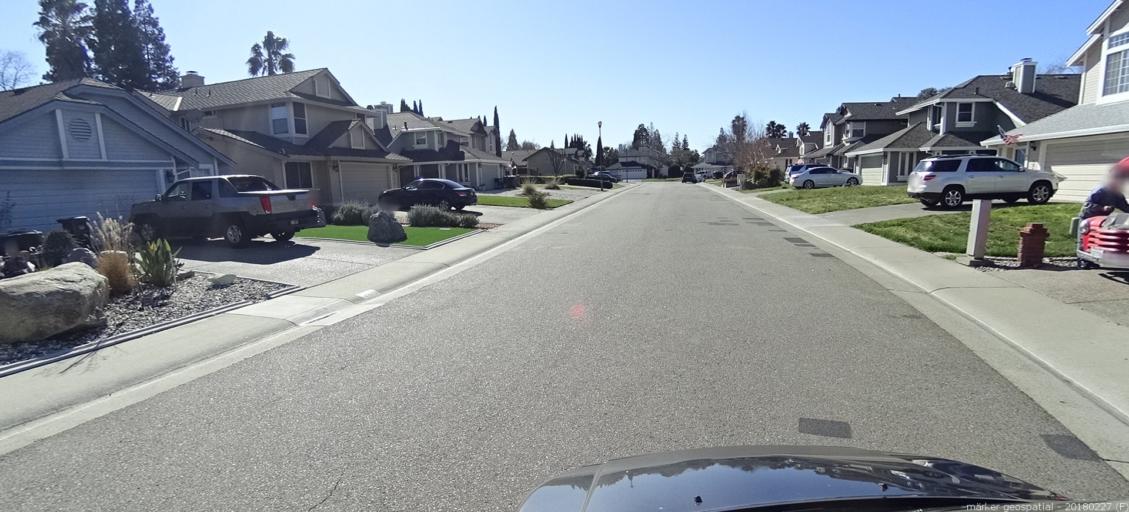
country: US
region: California
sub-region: Sacramento County
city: Antelope
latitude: 38.7230
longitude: -121.3497
